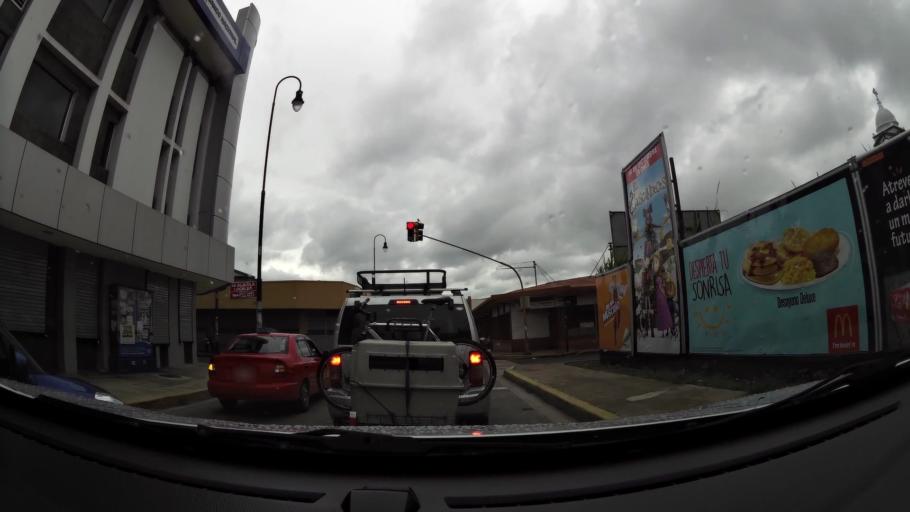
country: CR
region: San Jose
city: San Jose
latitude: 9.9298
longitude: -84.0796
